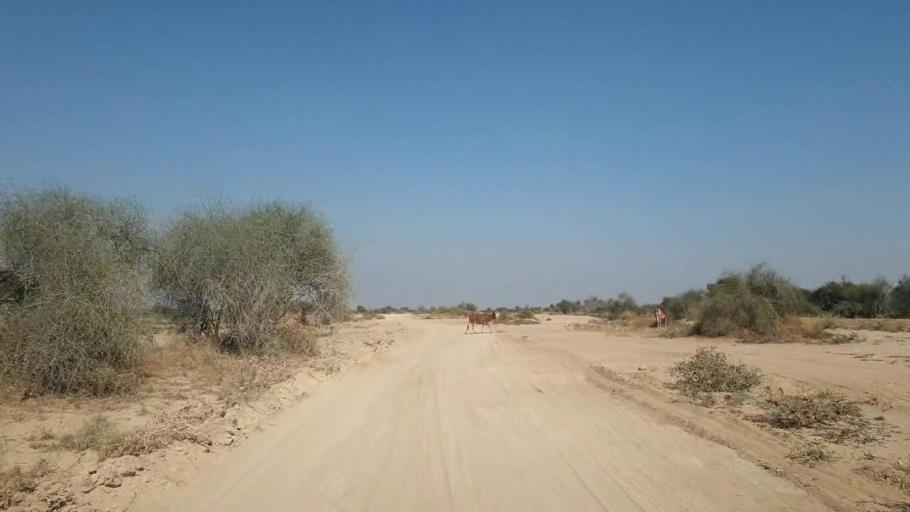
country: PK
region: Sindh
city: Jamshoro
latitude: 25.2721
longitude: 67.8066
